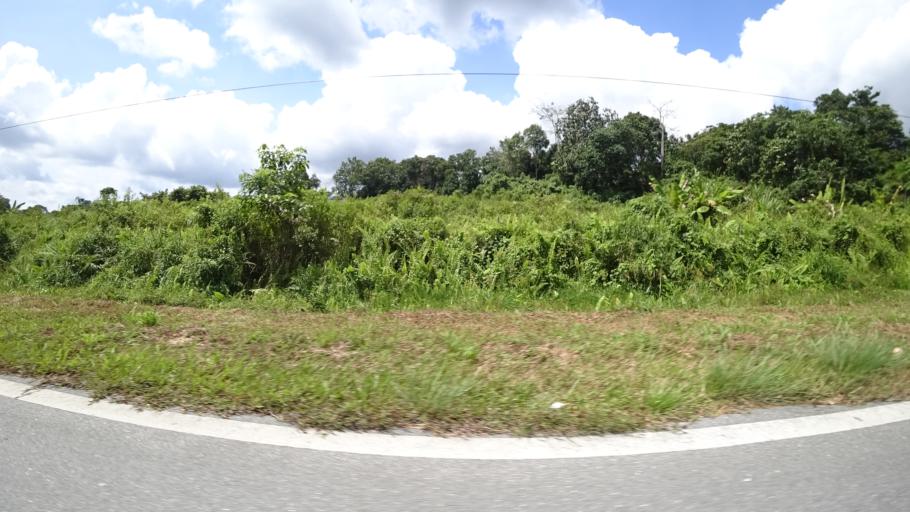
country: BN
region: Tutong
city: Tutong
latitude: 4.7087
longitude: 114.7960
